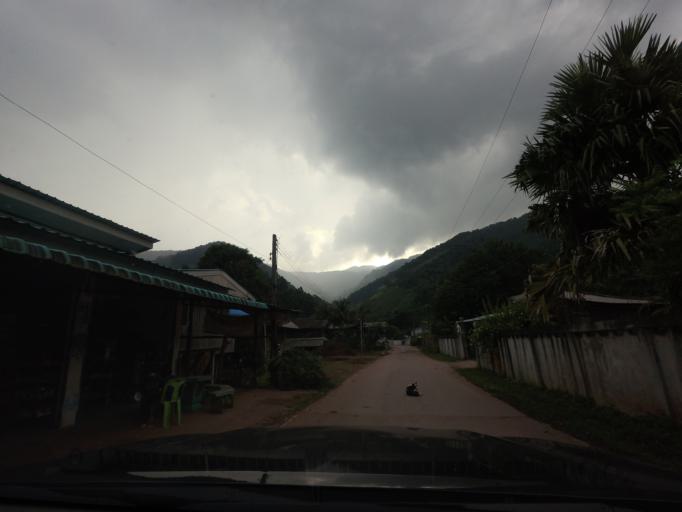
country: TH
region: Nan
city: Bo Kluea
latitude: 19.3524
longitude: 101.1605
